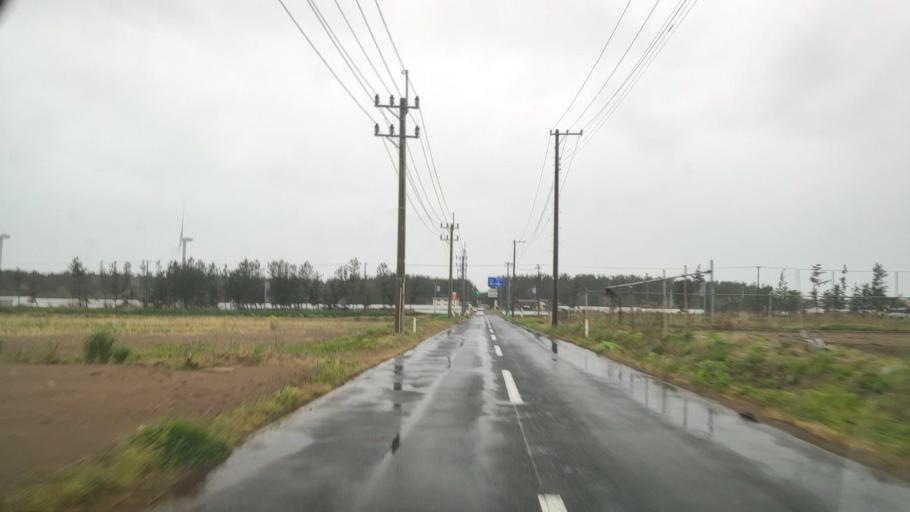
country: JP
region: Akita
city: Noshiromachi
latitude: 40.0972
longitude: 139.9687
